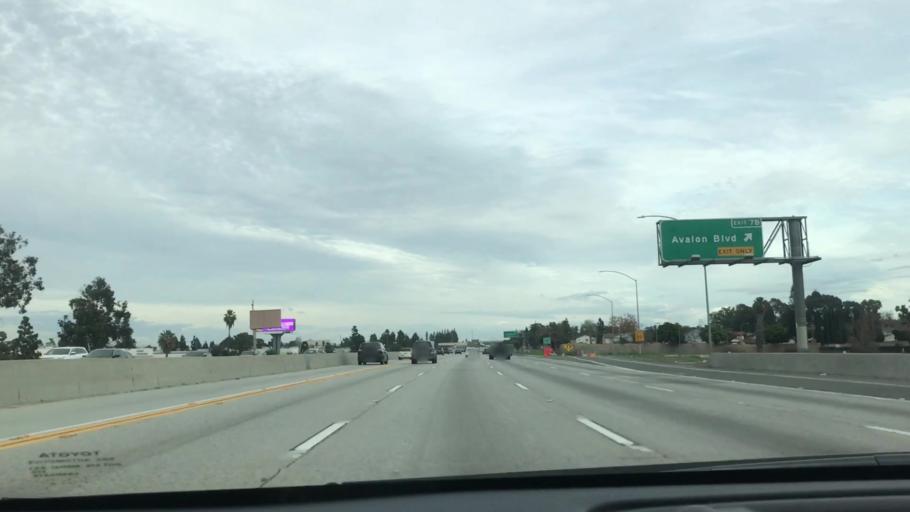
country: US
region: California
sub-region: Los Angeles County
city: West Rancho Dominguez
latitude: 33.8744
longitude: -118.2666
